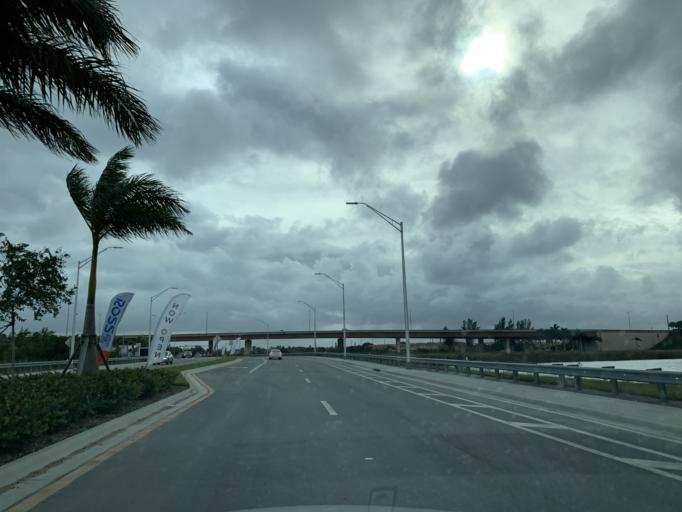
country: US
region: Florida
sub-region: Miami-Dade County
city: Tamiami
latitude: 25.7852
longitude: -80.3907
